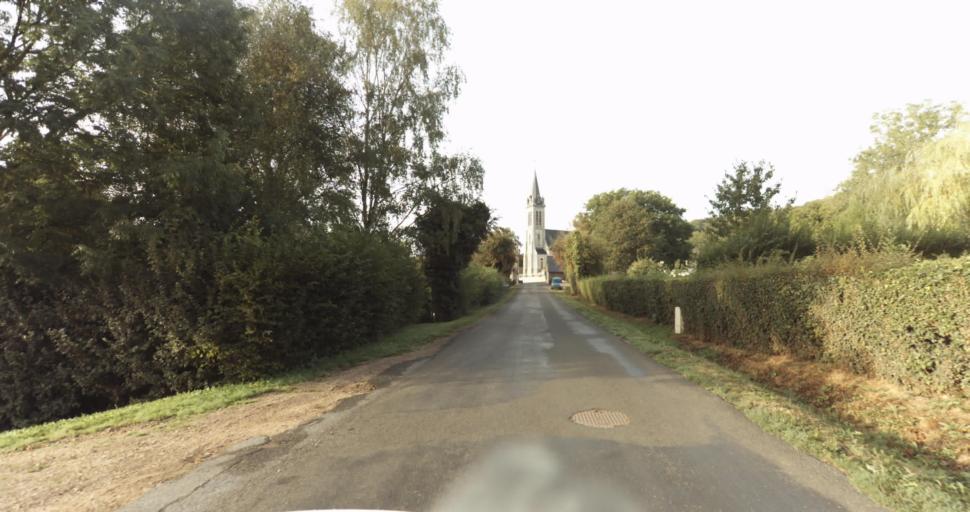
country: FR
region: Lower Normandy
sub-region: Departement de l'Orne
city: Vimoutiers
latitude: 48.9096
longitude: 0.2649
